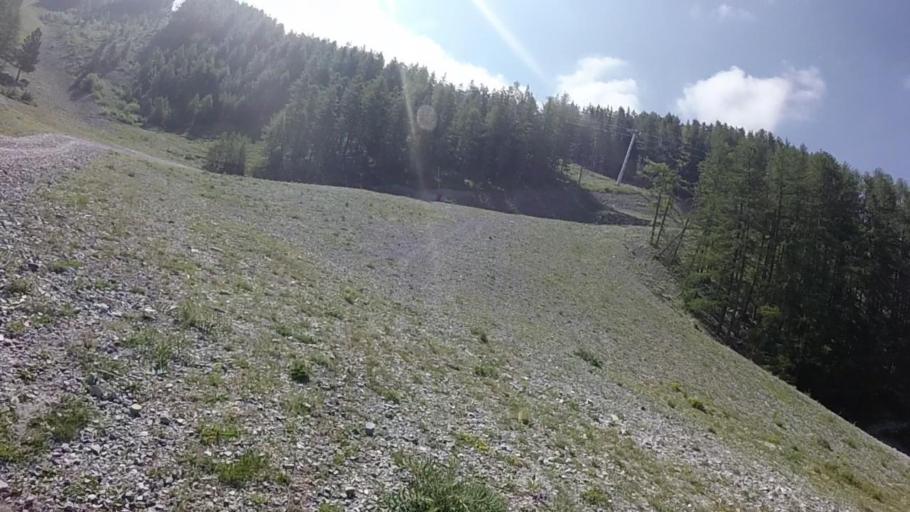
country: FR
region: Provence-Alpes-Cote d'Azur
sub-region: Departement des Alpes-de-Haute-Provence
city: Seyne-les-Alpes
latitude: 44.4054
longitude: 6.3702
